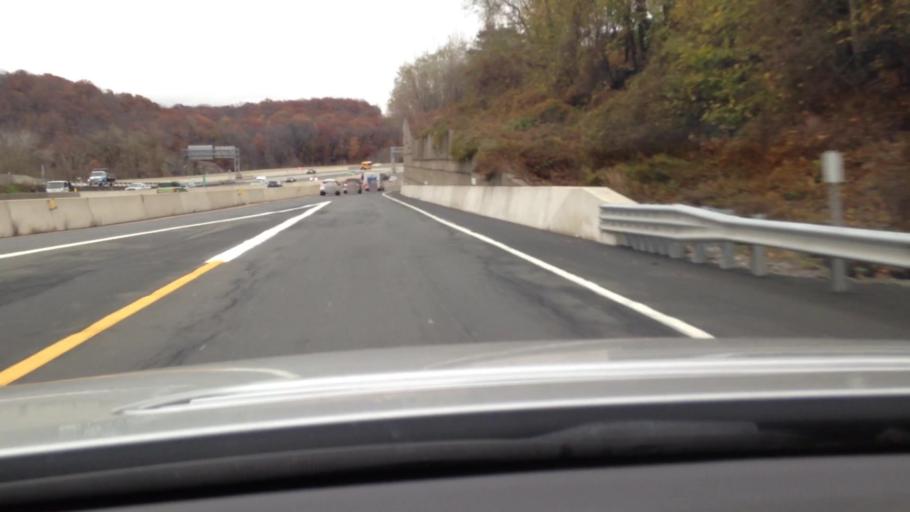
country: US
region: New York
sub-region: Westchester County
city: Elmsford
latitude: 41.0574
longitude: -73.8325
